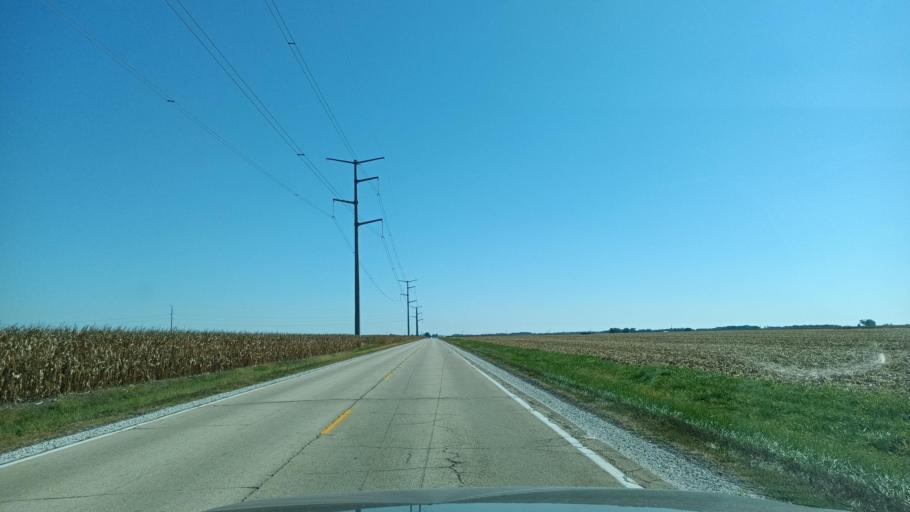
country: US
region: Illinois
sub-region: Peoria County
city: Elmwood
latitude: 40.9022
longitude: -89.9833
